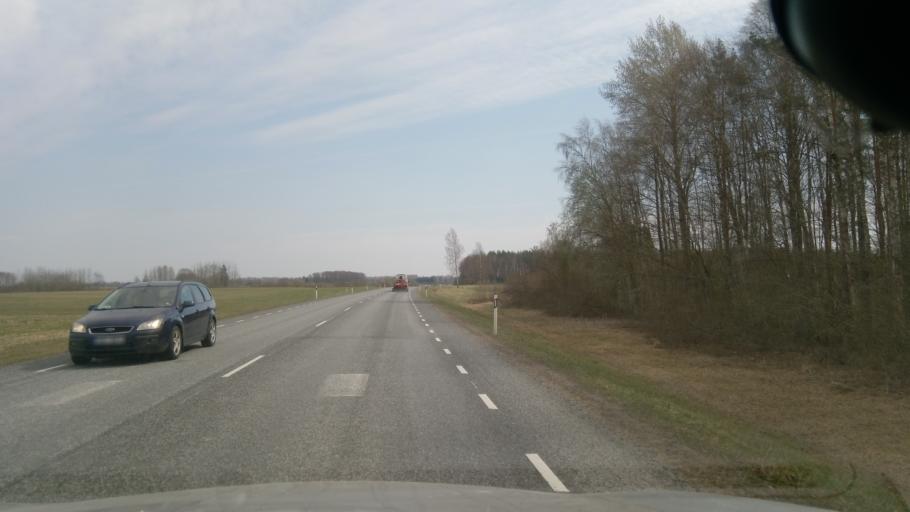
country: EE
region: Jaervamaa
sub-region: Tueri vald
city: Sarevere
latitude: 58.7781
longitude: 25.4987
